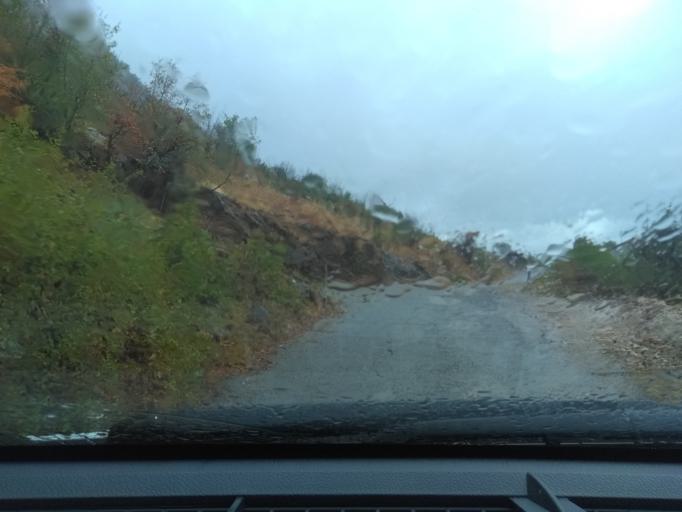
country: ME
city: Stari Bar
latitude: 42.1727
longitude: 19.1880
